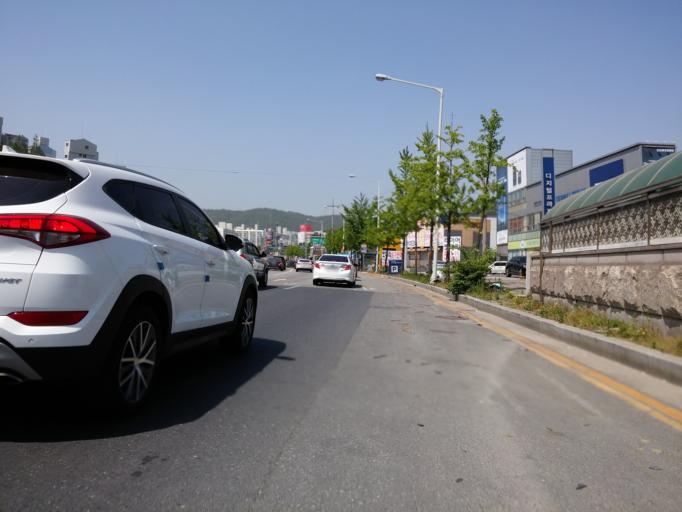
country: KR
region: Daejeon
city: Daejeon
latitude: 36.3017
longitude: 127.3305
